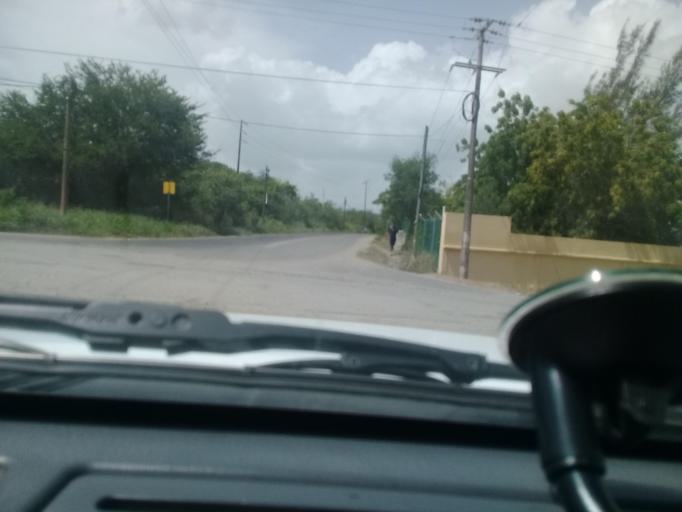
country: MX
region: Veracruz
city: Anahuac
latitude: 22.2252
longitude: -97.8337
